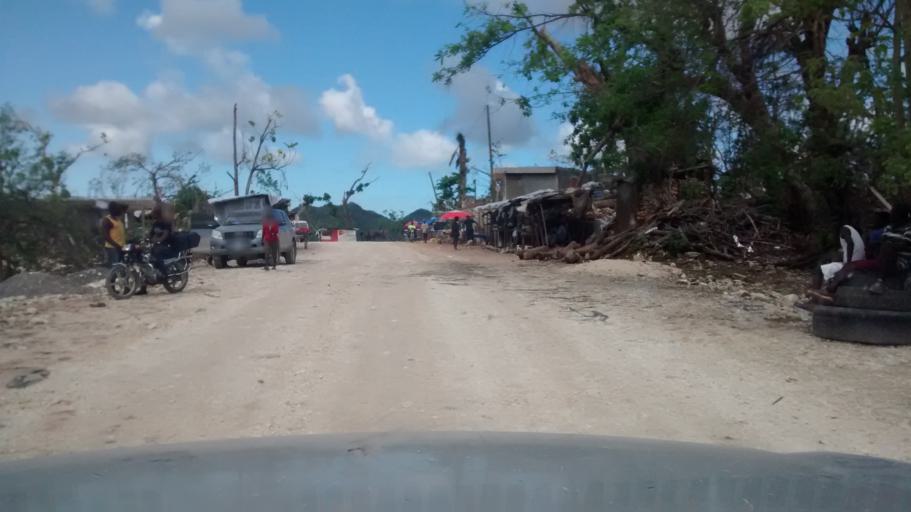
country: HT
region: Grandans
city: Corail
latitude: 18.5337
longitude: -73.9943
